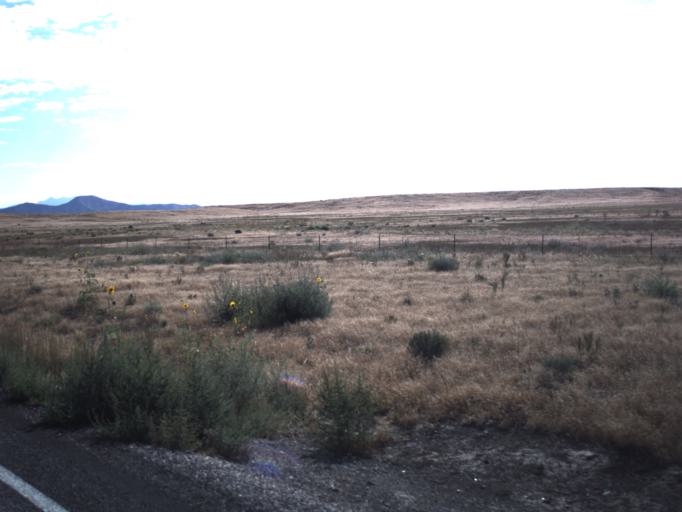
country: US
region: Utah
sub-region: Juab County
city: Nephi
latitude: 39.6911
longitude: -112.2350
